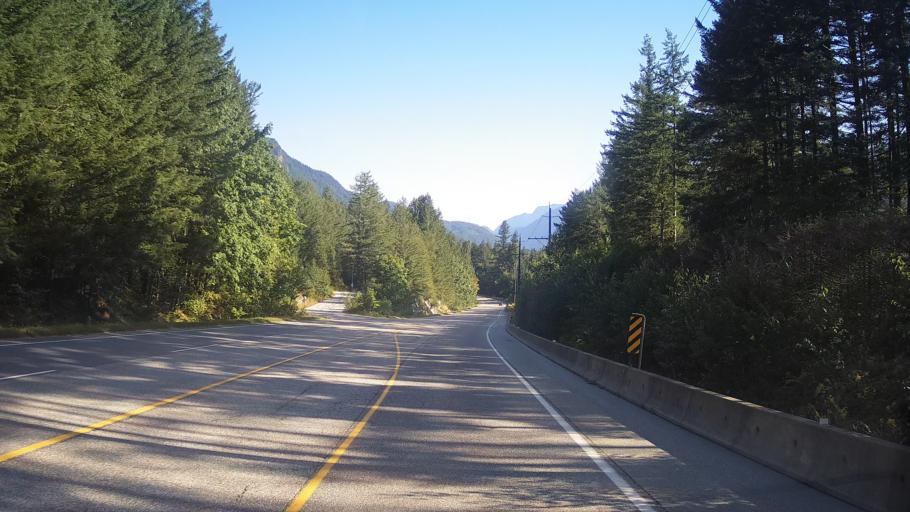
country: CA
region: British Columbia
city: Hope
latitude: 49.4252
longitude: -121.4385
